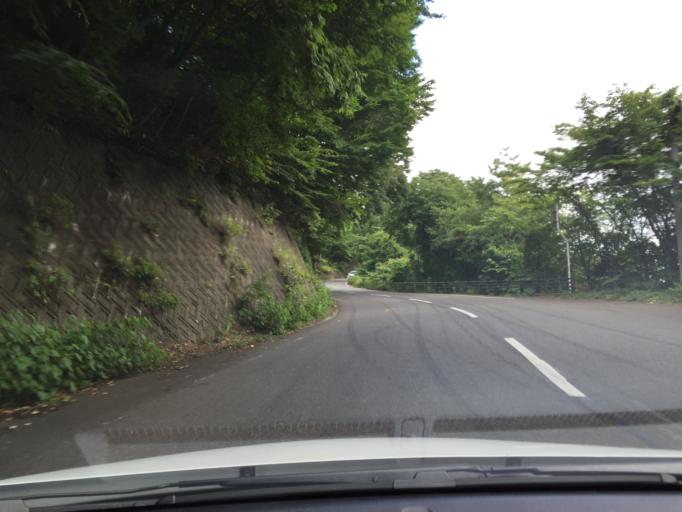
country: JP
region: Fukushima
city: Sukagawa
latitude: 37.2658
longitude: 140.1164
